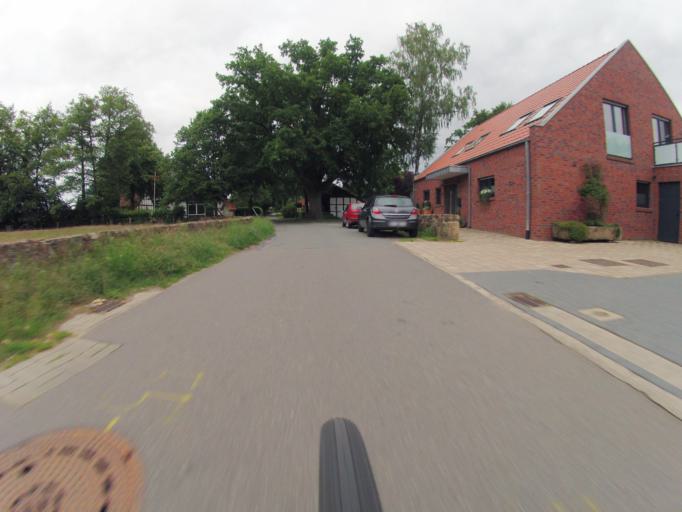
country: DE
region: North Rhine-Westphalia
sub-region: Regierungsbezirk Munster
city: Dreierwalde
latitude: 52.2417
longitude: 7.5249
